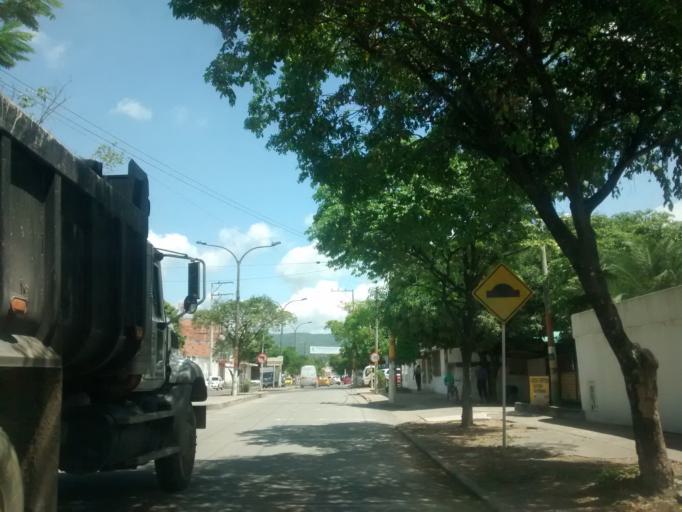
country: CO
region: Cundinamarca
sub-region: Girardot
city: Girardot City
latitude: 4.3021
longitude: -74.8000
